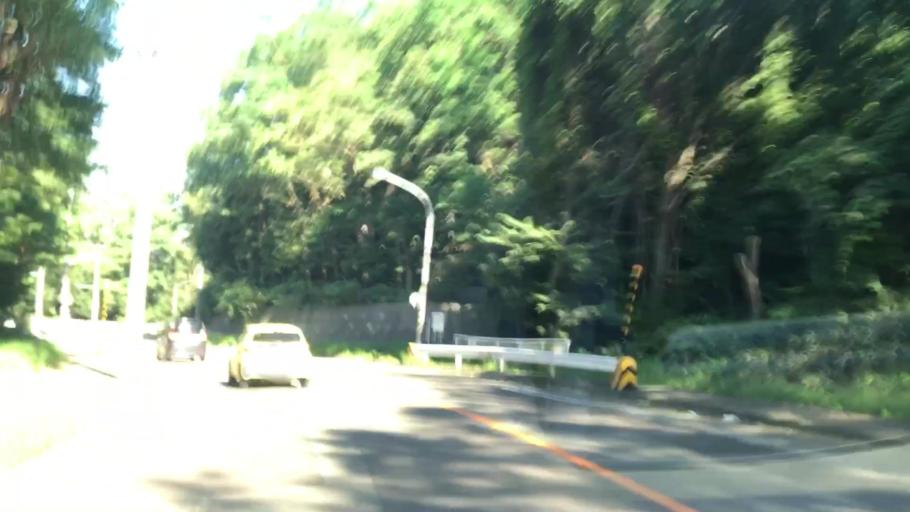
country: JP
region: Hokkaido
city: Sapporo
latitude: 43.0425
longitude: 141.3128
